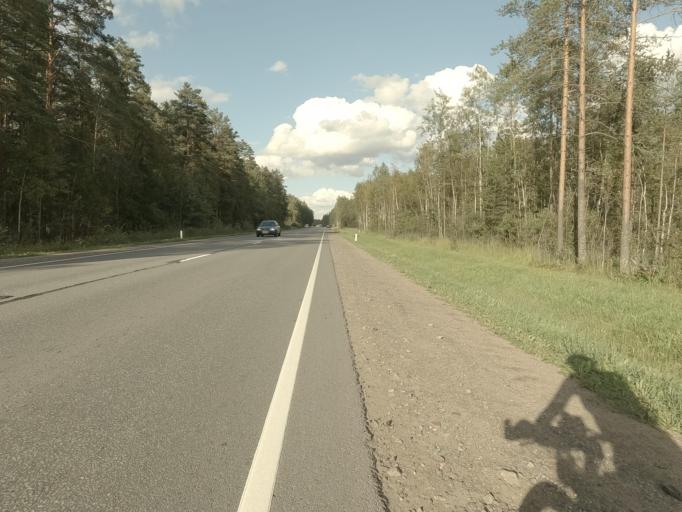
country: RU
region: Leningrad
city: Mga
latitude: 59.7101
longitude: 31.0227
